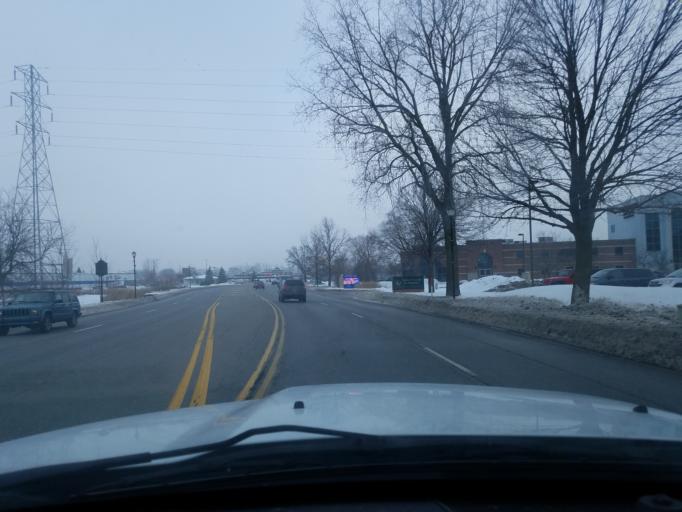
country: US
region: Indiana
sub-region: Saint Joseph County
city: Mishawaka
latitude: 41.6954
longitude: -86.1819
